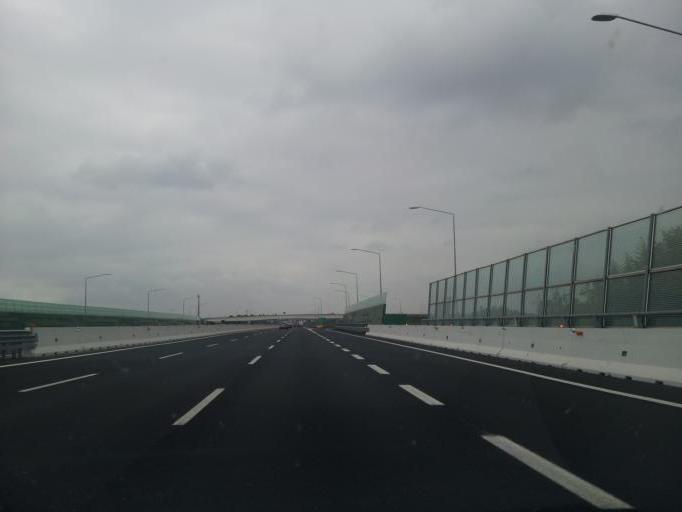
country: IT
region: Veneto
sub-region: Provincia di Venezia
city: Meolo
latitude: 45.6255
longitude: 12.4342
